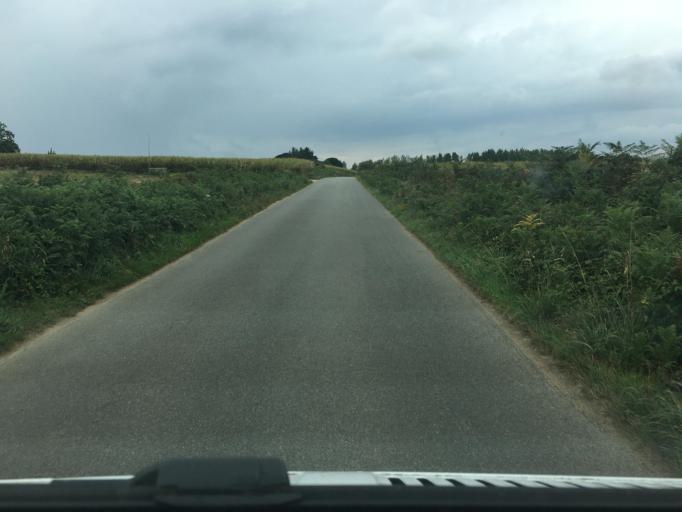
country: FR
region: Brittany
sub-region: Departement du Finistere
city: Beuzec-Cap-Sizun
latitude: 48.0758
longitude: -4.4757
